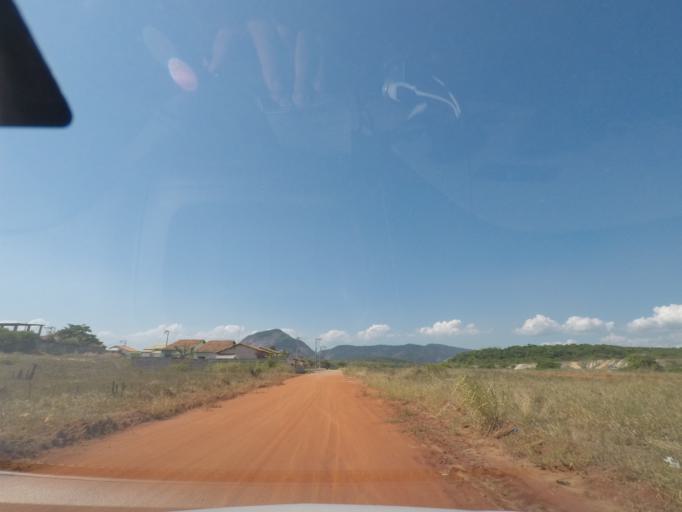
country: BR
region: Rio de Janeiro
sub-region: Marica
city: Marica
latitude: -22.9677
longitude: -42.9038
